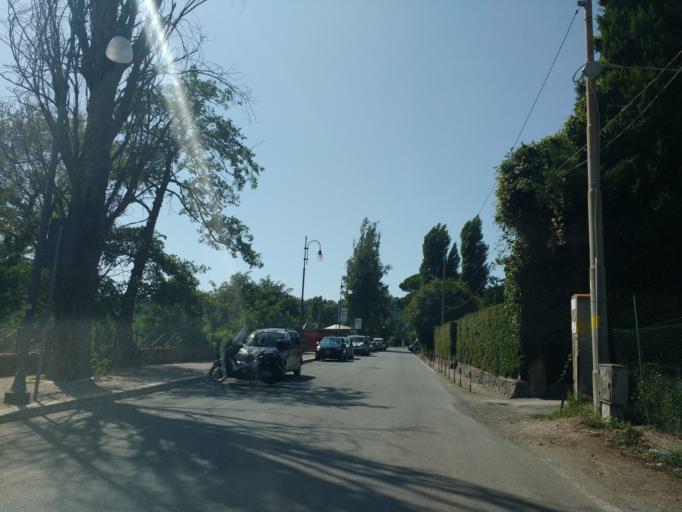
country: IT
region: Latium
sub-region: Citta metropolitana di Roma Capitale
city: Castel Gandolfo
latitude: 41.7602
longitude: 12.6659
